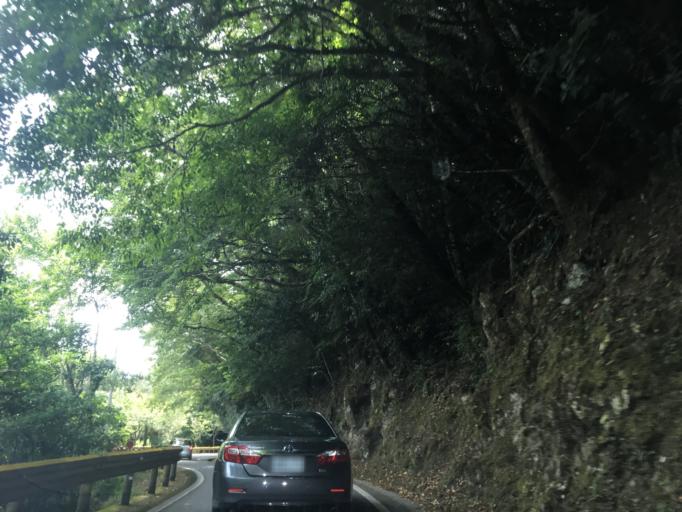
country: TW
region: Taiwan
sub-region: Hualien
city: Hualian
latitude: 24.1804
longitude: 121.3939
